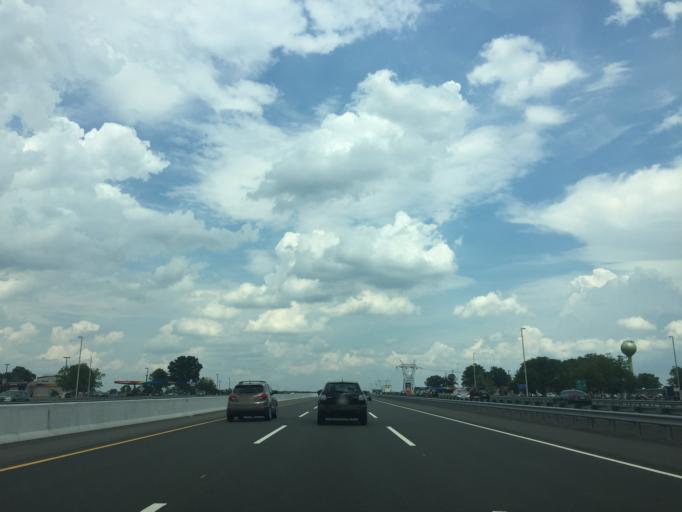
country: US
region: New Jersey
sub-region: Mercer County
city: Yardville
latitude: 40.1752
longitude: -74.6332
